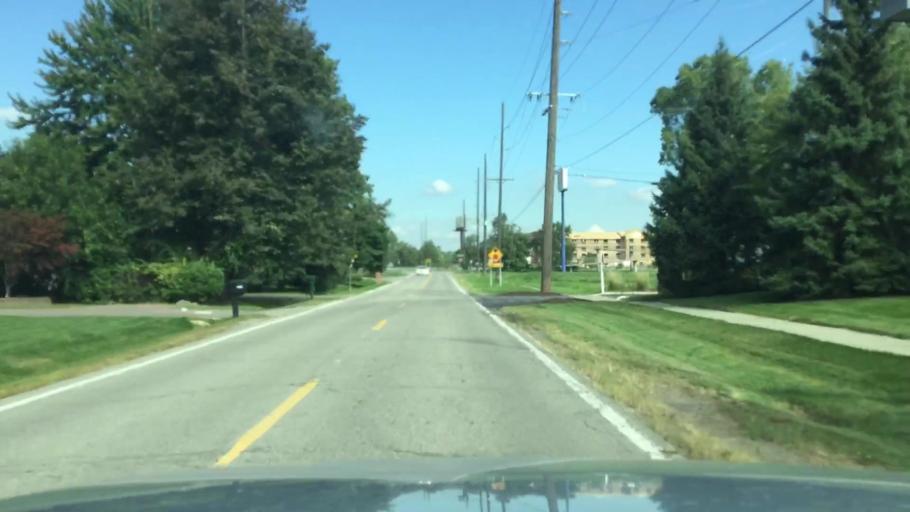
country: US
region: Michigan
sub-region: Wayne County
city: Belleville
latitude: 42.2171
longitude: -83.4942
